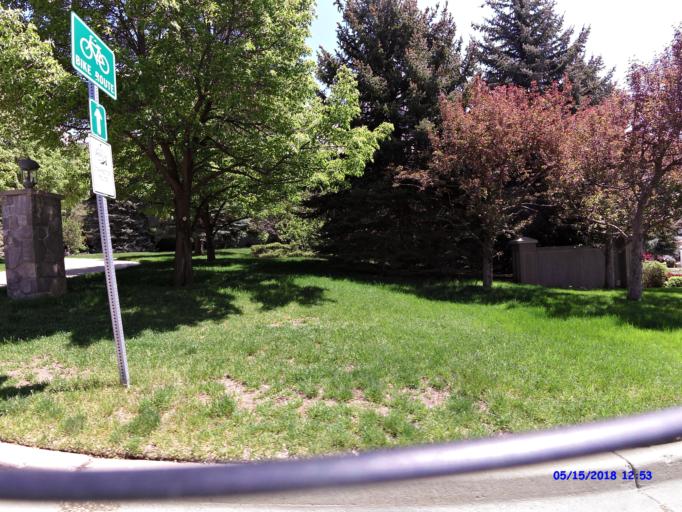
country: US
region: Utah
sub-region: Weber County
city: Uintah
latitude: 41.1578
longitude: -111.9233
